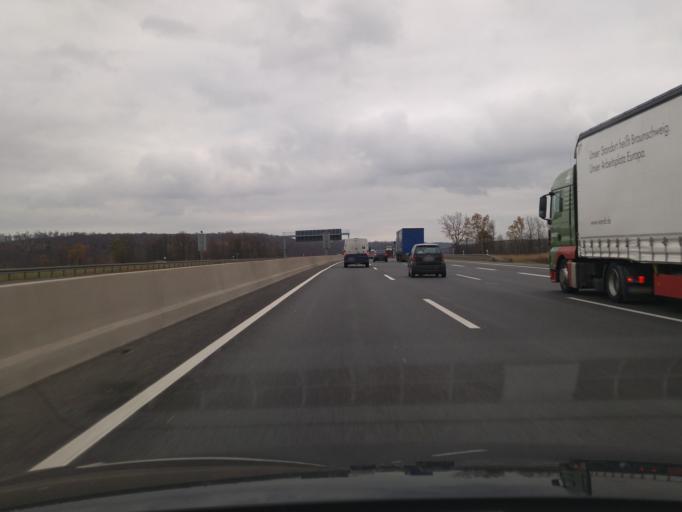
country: DE
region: Lower Saxony
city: Haverlah
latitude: 52.0807
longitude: 10.1880
